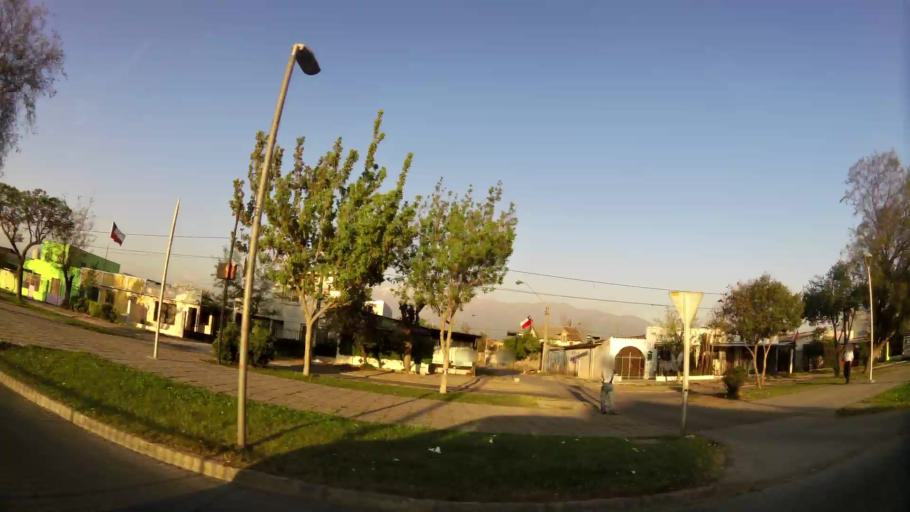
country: CL
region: Santiago Metropolitan
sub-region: Provincia de Santiago
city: Santiago
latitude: -33.5170
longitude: -70.6237
